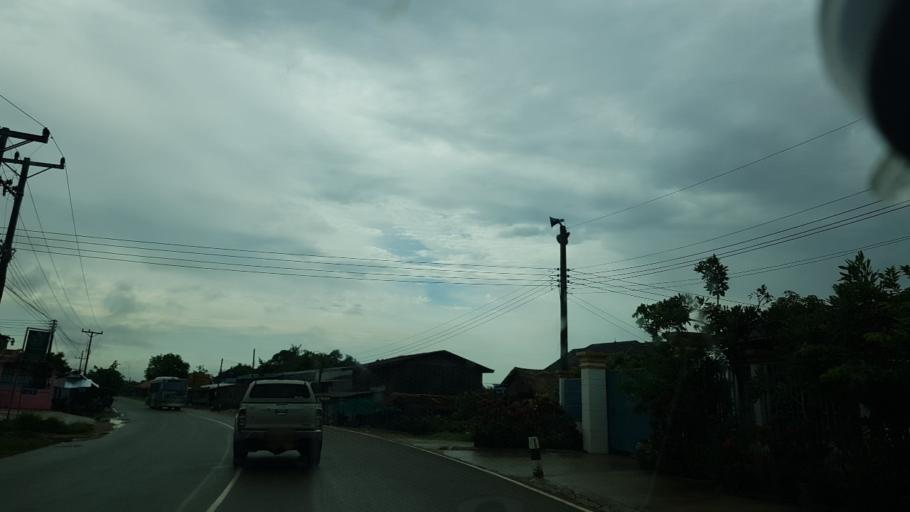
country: TH
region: Nong Khai
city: Pho Tak
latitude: 17.9826
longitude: 102.4472
